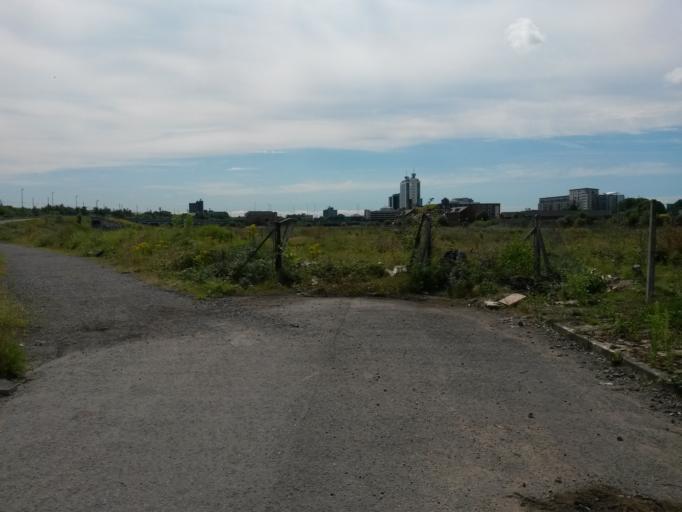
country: GB
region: England
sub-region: Manchester
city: Hulme
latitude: 53.4693
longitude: -2.2707
